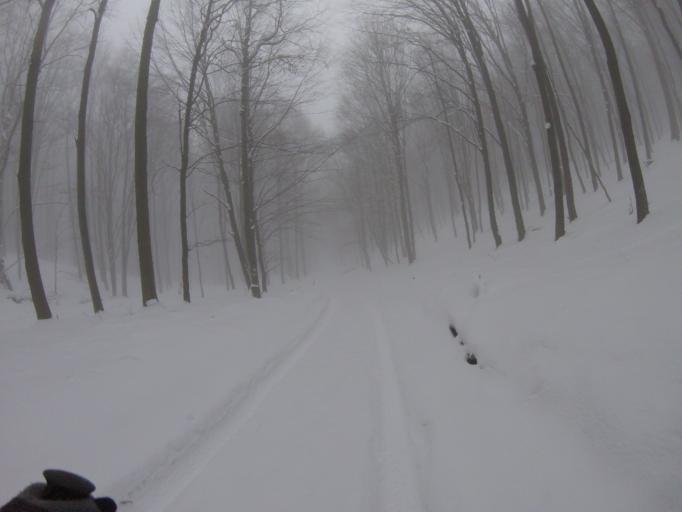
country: HU
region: Heves
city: Szilvasvarad
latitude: 48.0639
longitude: 20.4198
